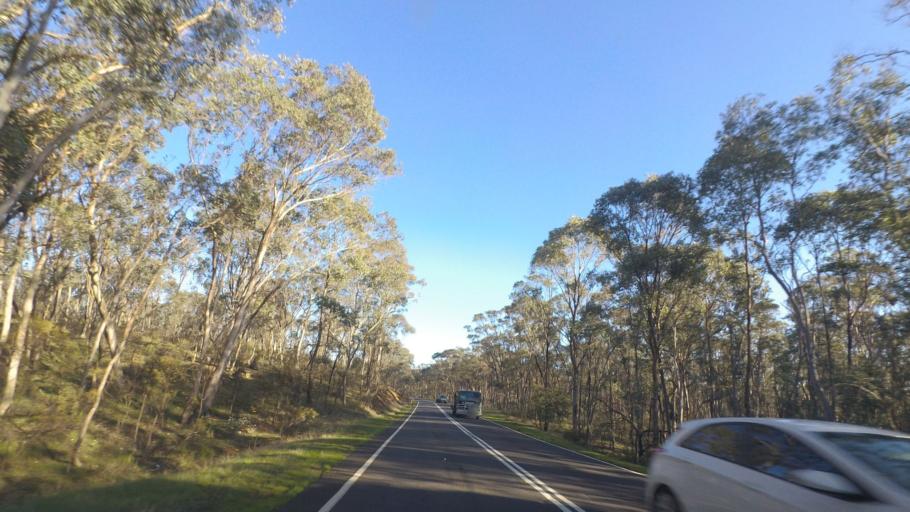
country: AU
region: Victoria
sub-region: Greater Bendigo
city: Kennington
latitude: -36.9167
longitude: 144.4920
